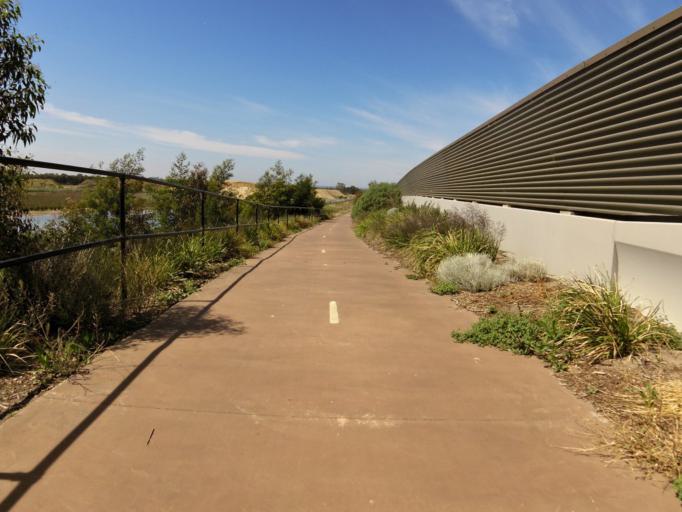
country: AU
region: Victoria
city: Heatherton
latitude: -37.9488
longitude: 145.1004
